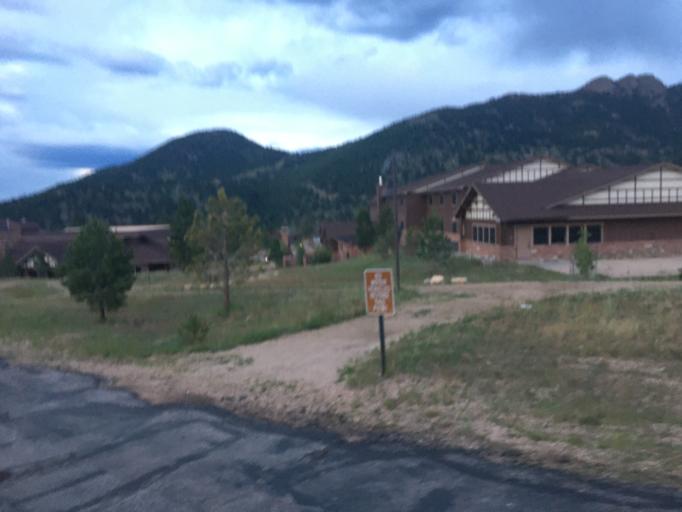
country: US
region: Colorado
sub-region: Larimer County
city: Estes Park
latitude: 40.3389
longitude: -105.5747
